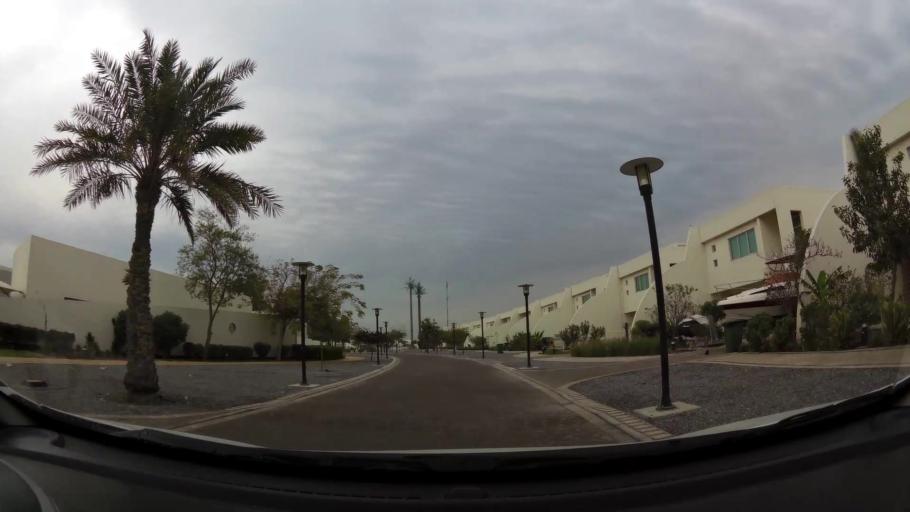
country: BH
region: Central Governorate
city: Dar Kulayb
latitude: 25.8385
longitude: 50.6166
